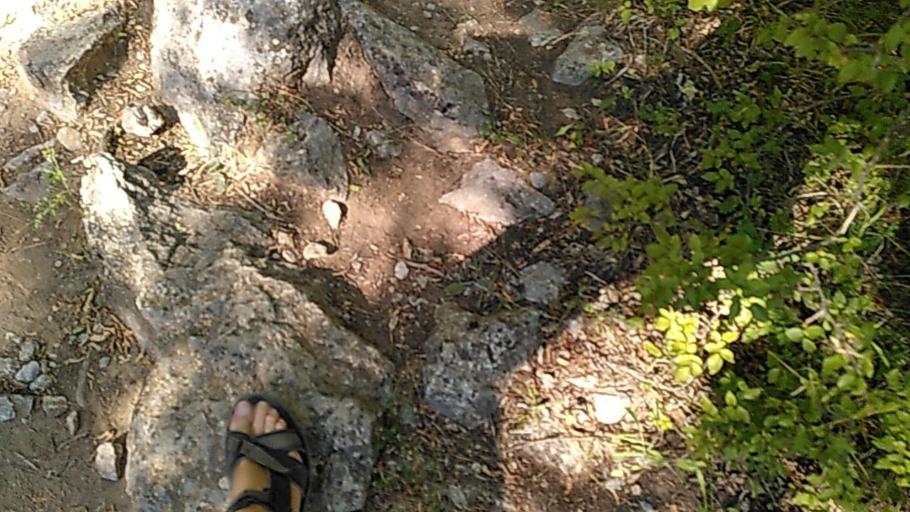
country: HR
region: Zadarska
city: Starigrad
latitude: 44.3089
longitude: 15.4789
